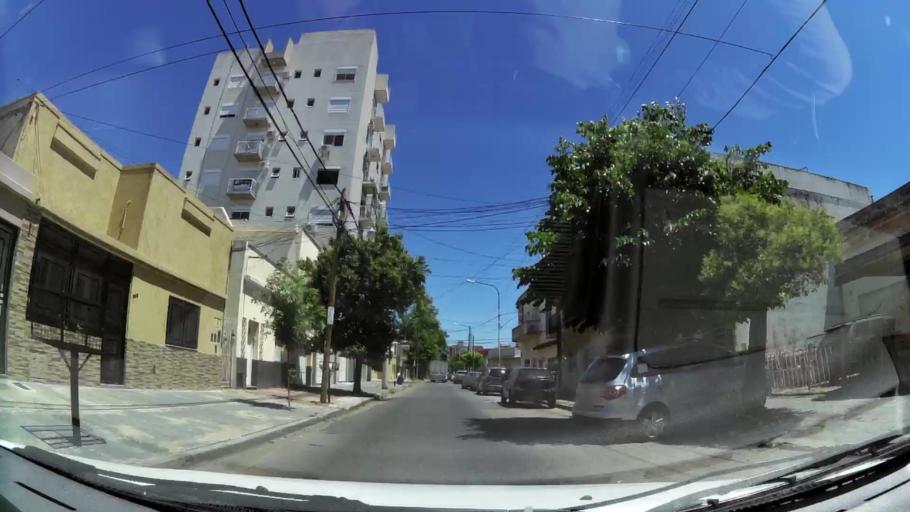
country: AR
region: Buenos Aires
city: Caseros
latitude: -34.5968
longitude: -58.5362
